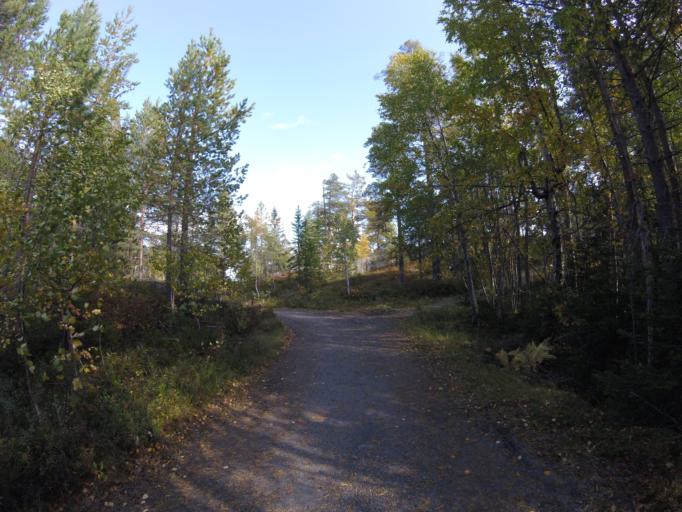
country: NO
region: Buskerud
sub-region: Kongsberg
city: Kongsberg
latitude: 59.6654
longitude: 9.5809
